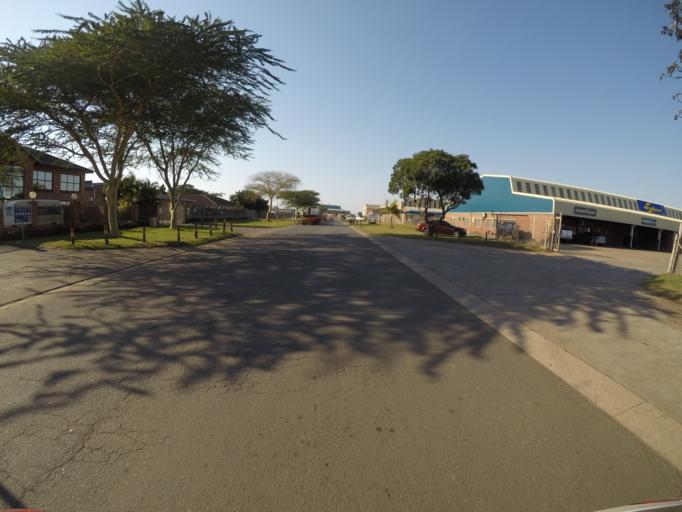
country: ZA
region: KwaZulu-Natal
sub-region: uThungulu District Municipality
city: Richards Bay
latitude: -28.7512
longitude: 32.0232
